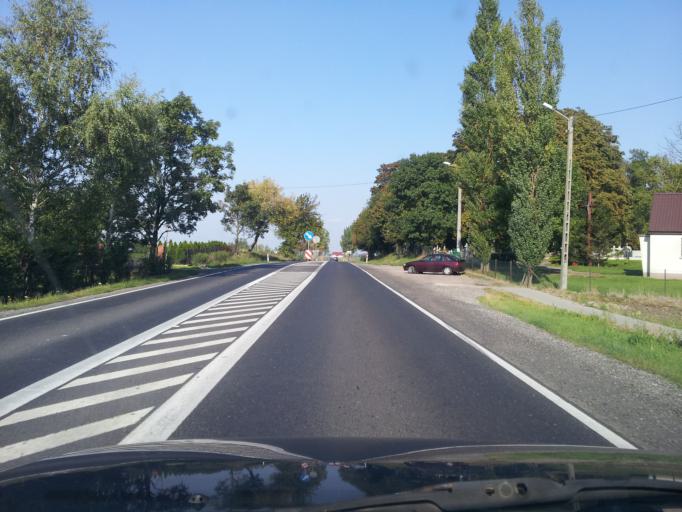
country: PL
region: Kujawsko-Pomorskie
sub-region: Powiat inowroclawski
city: Wierzchoslawice
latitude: 52.8490
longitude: 18.3421
